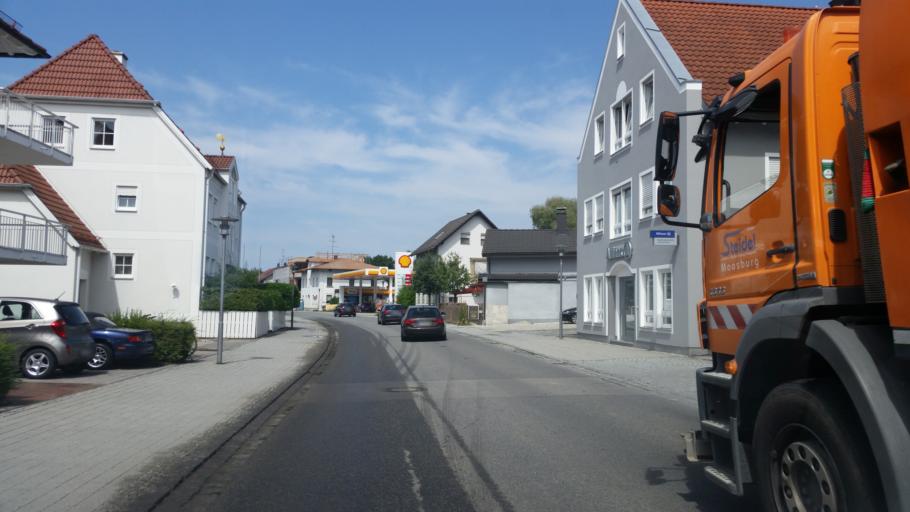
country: DE
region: Bavaria
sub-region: Lower Bavaria
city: Geisenhausen
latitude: 48.4746
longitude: 12.2566
